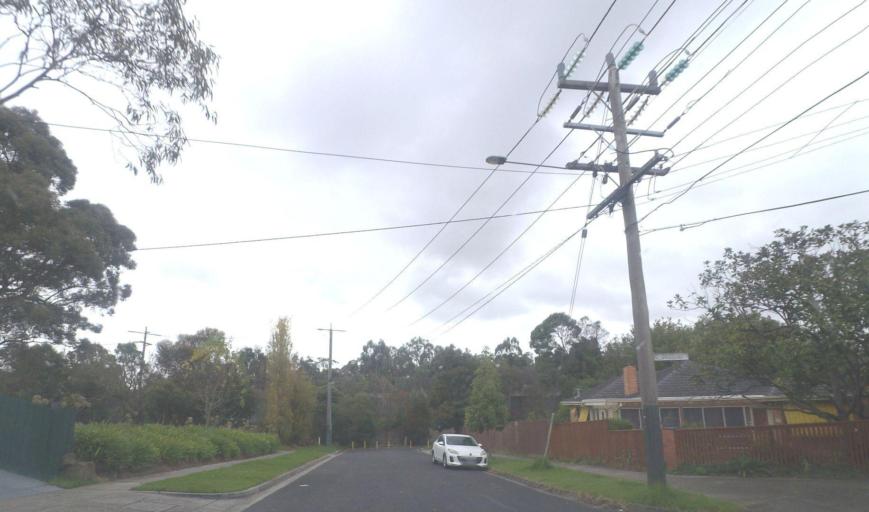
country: AU
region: Victoria
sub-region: Whitehorse
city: Blackburn North
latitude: -37.8015
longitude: 145.1536
